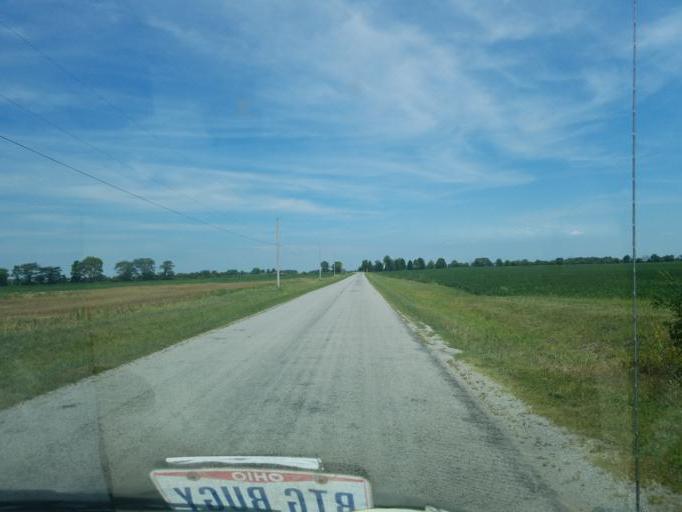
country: US
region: Ohio
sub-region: Madison County
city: West Jefferson
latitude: 39.8899
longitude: -83.3136
